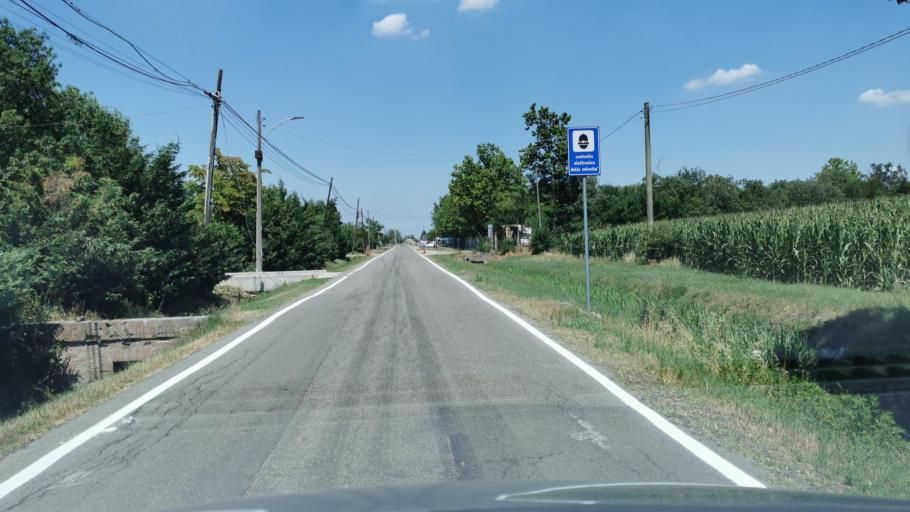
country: IT
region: Emilia-Romagna
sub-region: Provincia di Modena
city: Fossoli
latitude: 44.8266
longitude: 10.9006
